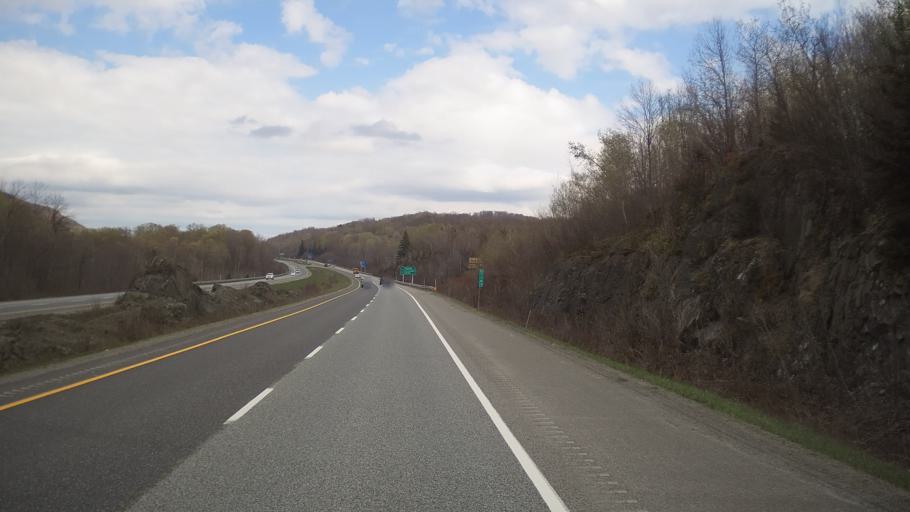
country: CA
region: Quebec
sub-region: Estrie
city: Magog
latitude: 45.2893
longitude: -72.2582
